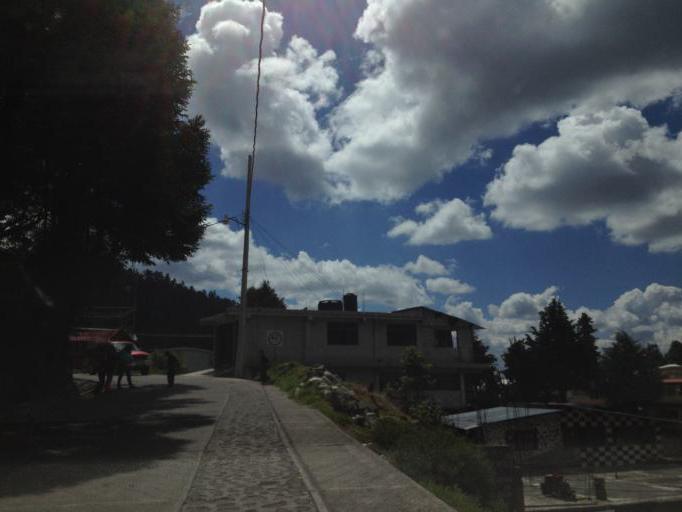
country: MX
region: Hidalgo
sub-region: Pachuca de Soto
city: San Miguel Cerezo (El Cerezo)
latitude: 20.2118
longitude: -98.6970
